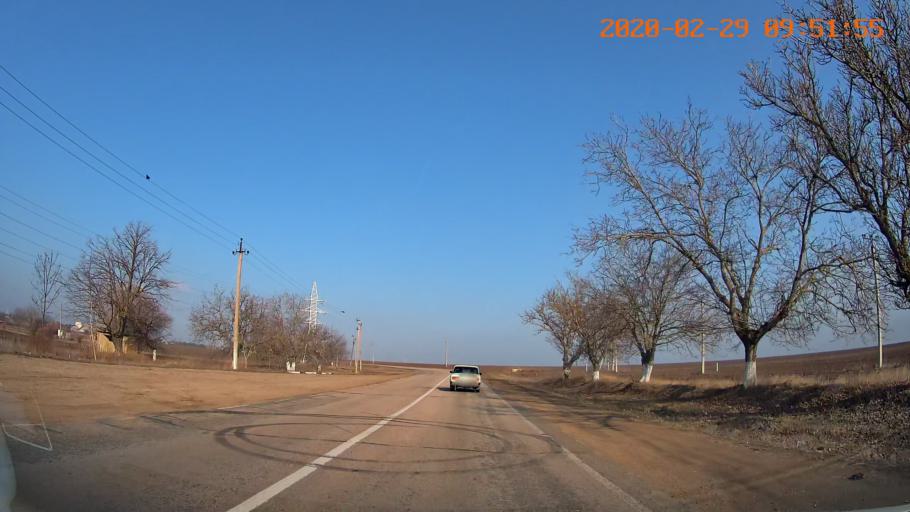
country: MD
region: Telenesti
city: Slobozia
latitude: 46.7127
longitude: 29.7349
